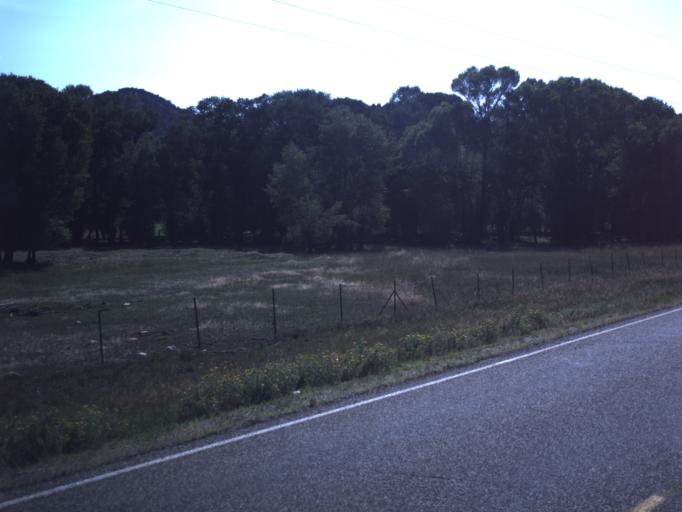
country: US
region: Utah
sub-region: Duchesne County
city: Duchesne
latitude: 40.3925
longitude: -110.7521
